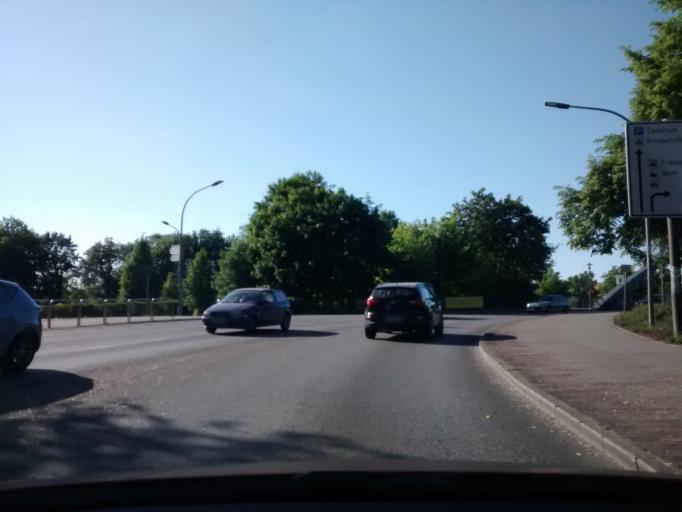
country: DE
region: Brandenburg
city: Furstenwalde
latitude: 52.3537
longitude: 14.0627
